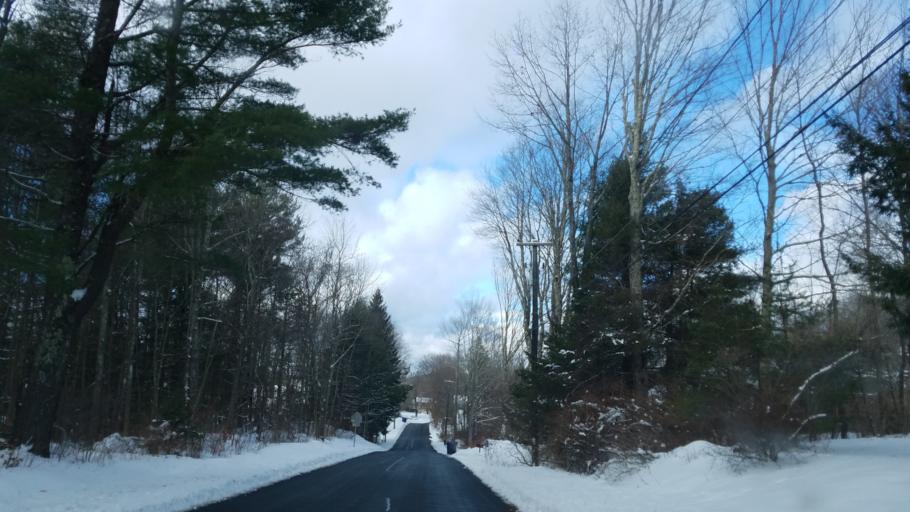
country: US
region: Connecticut
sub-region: Litchfield County
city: Winsted
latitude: 41.9876
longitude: -73.0929
